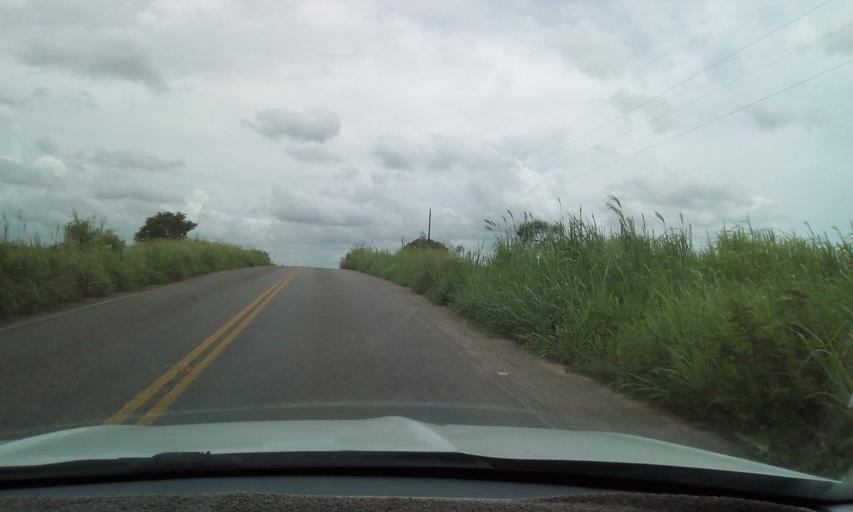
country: BR
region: Paraiba
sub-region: Gurinhem
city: Gurinhem
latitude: -7.1604
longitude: -35.3564
